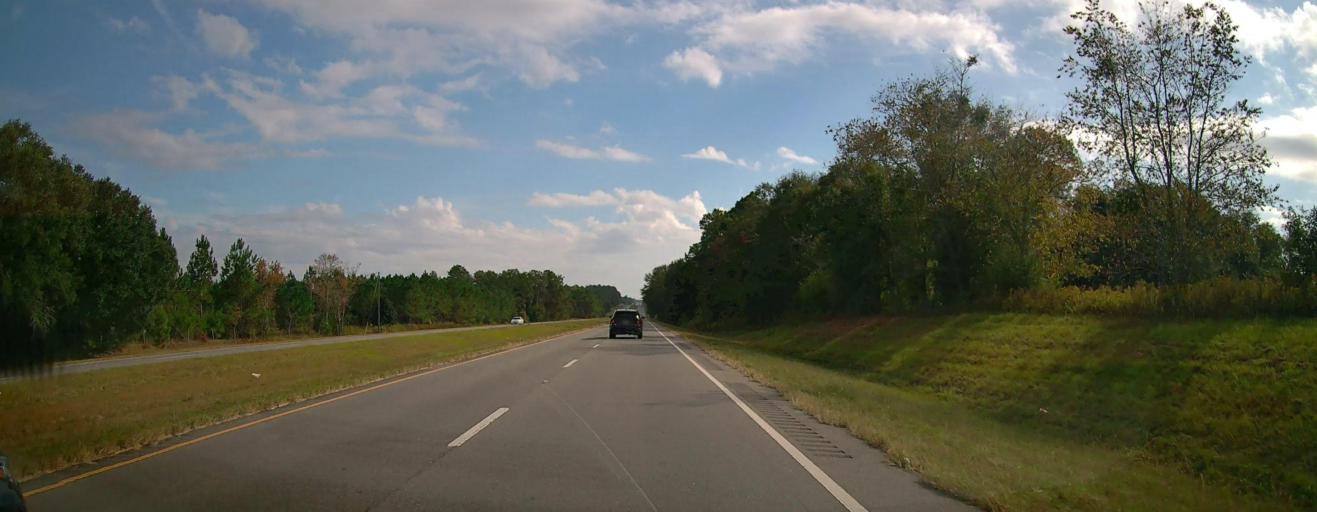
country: US
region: Georgia
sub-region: Thomas County
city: Meigs
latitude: 30.9889
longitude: -84.0427
